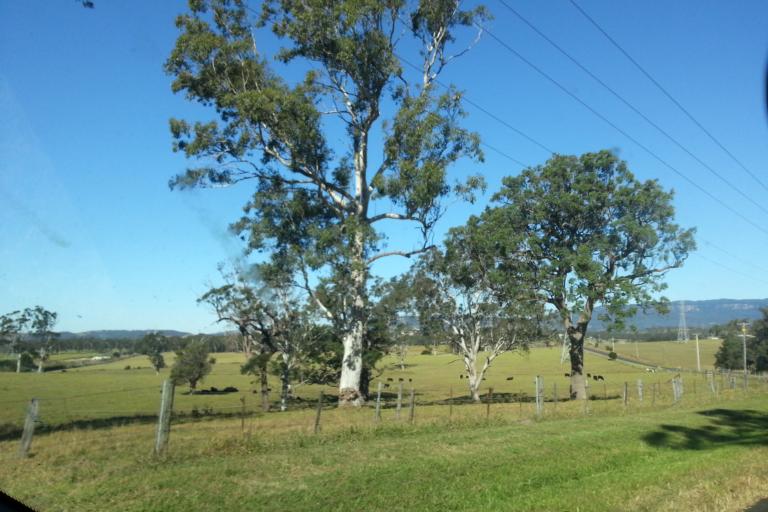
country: AU
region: New South Wales
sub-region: Wollongong
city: Dapto
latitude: -34.5191
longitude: 150.7808
